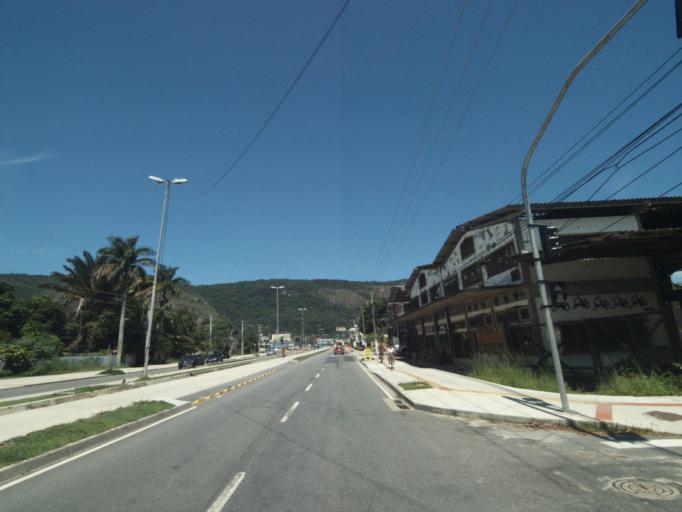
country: BR
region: Rio de Janeiro
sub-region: Niteroi
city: Niteroi
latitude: -22.9498
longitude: -43.0297
